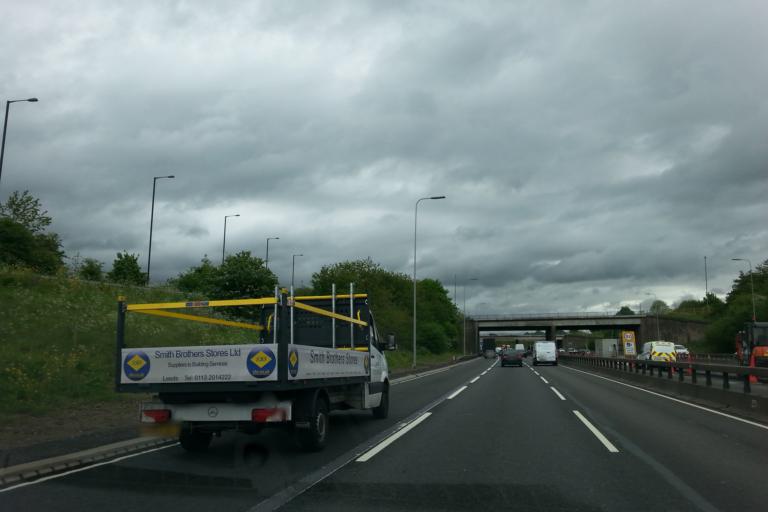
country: GB
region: England
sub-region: Manchester
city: Heywood
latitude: 53.5750
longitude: -2.2098
